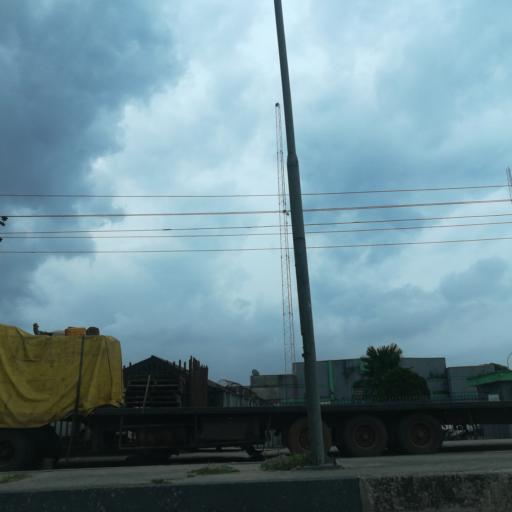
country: NG
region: Rivers
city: Port Harcourt
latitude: 4.8185
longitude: 7.0409
